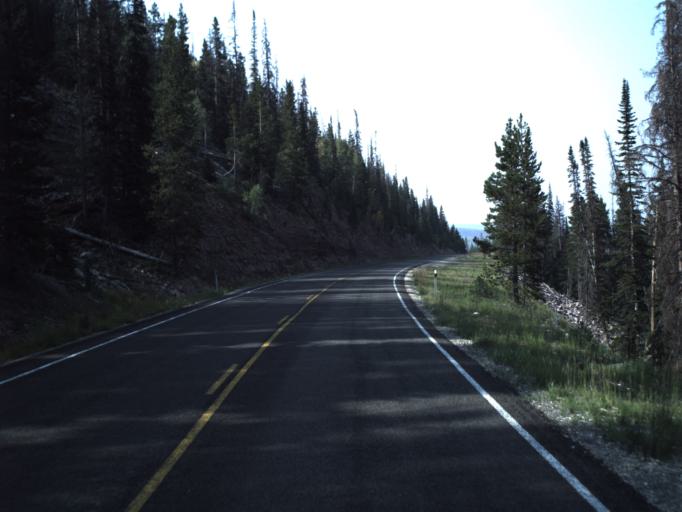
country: US
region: Utah
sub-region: Summit County
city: Kamas
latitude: 40.7718
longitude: -110.8841
